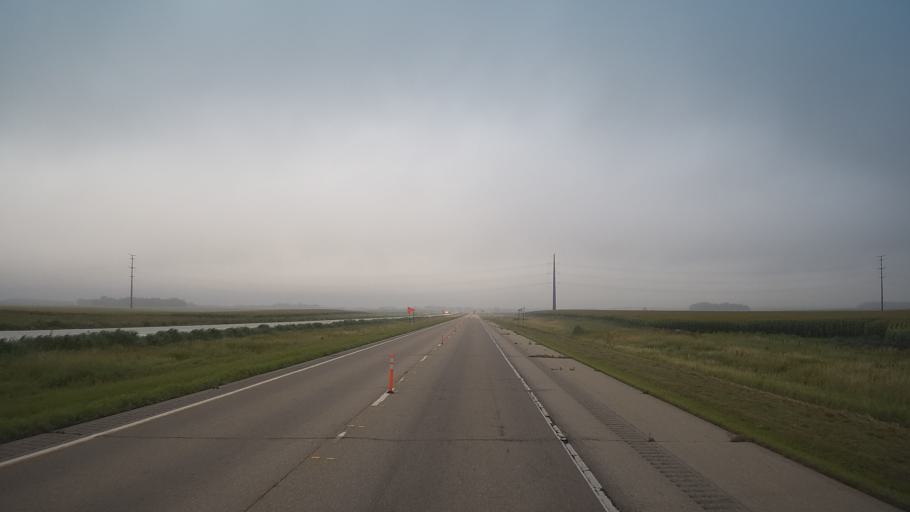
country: US
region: Minnesota
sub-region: Faribault County
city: Blue Earth
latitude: 43.6661
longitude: -94.1654
